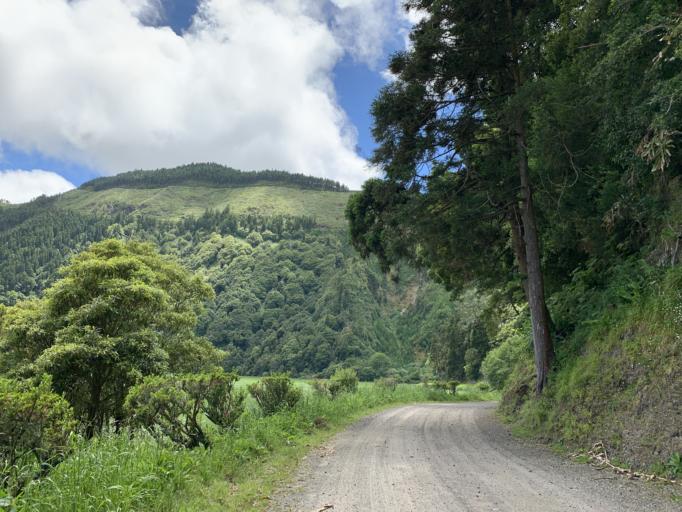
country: PT
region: Azores
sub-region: Ponta Delgada
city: Arrifes
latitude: 37.8468
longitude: -25.7935
